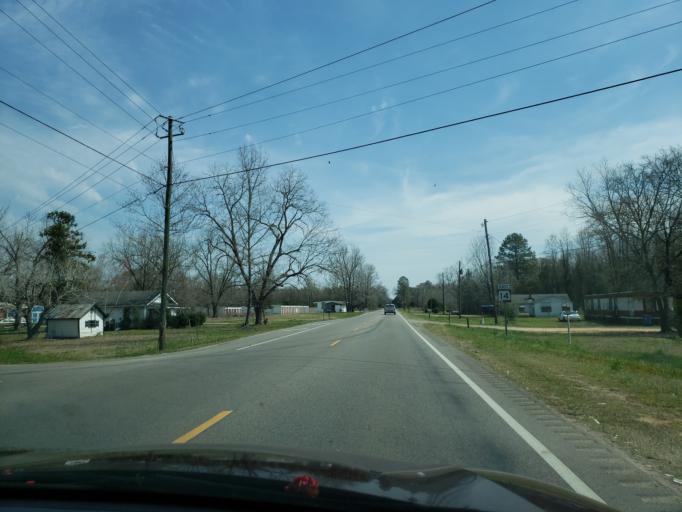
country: US
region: Alabama
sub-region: Autauga County
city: Prattville
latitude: 32.4308
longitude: -86.5035
